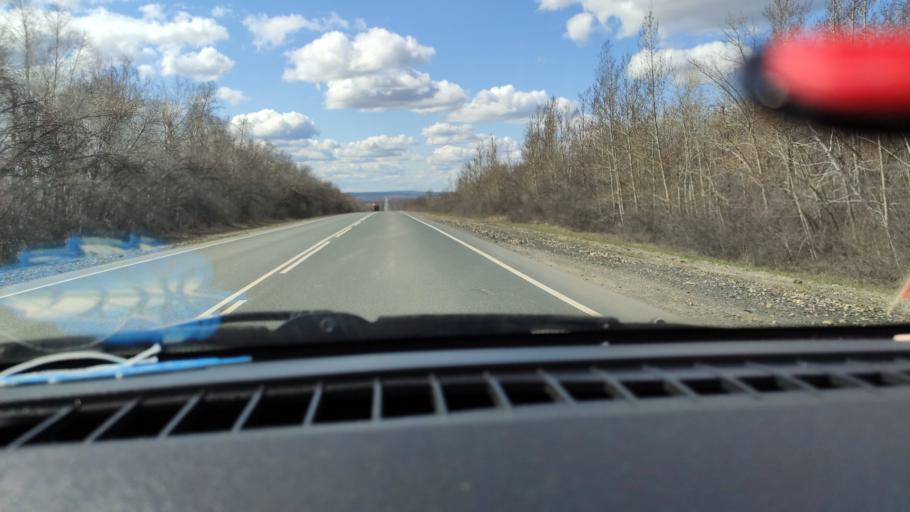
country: RU
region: Saratov
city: Khvalynsk
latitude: 52.6176
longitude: 48.1680
